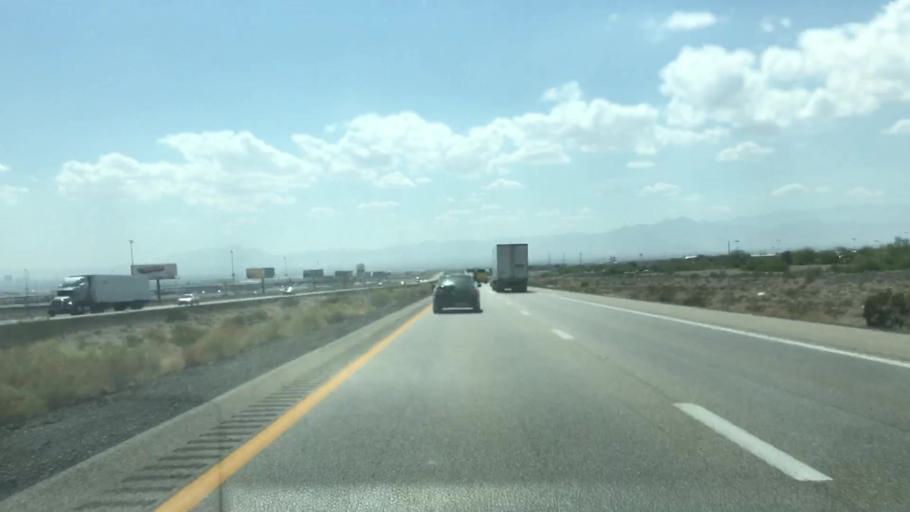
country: US
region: Nevada
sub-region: Clark County
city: Nellis Air Force Base
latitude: 36.2890
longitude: -115.0106
